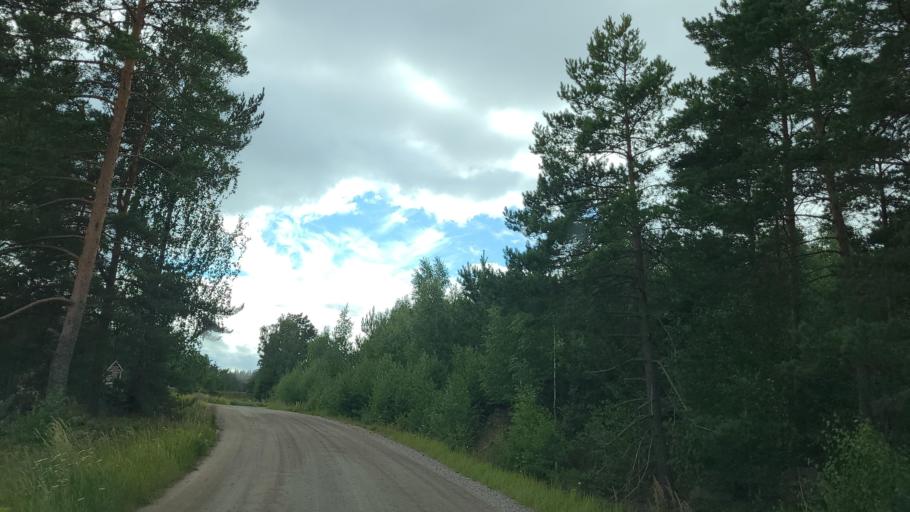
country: FI
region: Varsinais-Suomi
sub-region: Aboland-Turunmaa
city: Nagu
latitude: 60.2058
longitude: 21.8197
